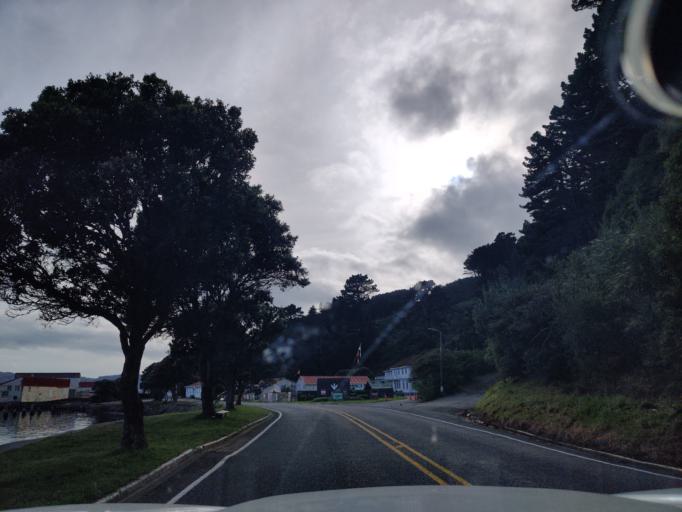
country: NZ
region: Wellington
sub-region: Wellington City
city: Wellington
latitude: -41.2965
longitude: 174.8222
